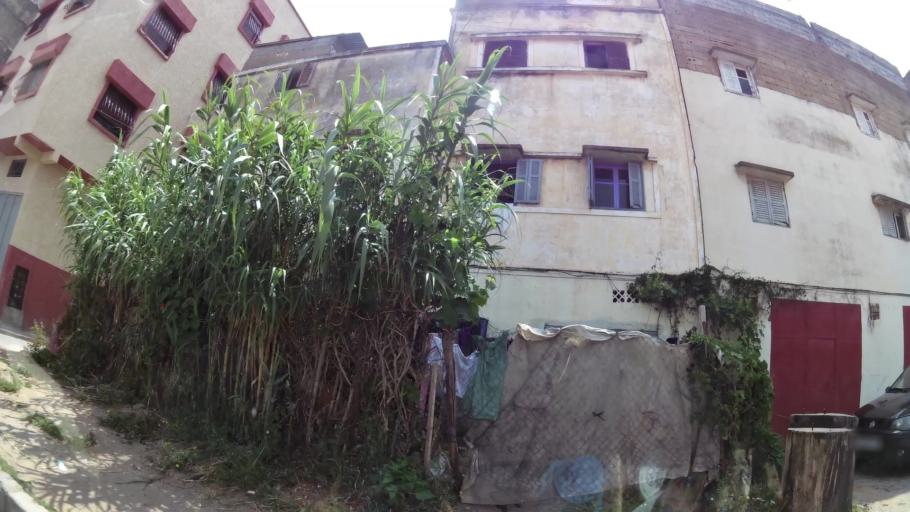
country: MA
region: Rabat-Sale-Zemmour-Zaer
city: Sale
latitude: 34.0533
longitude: -6.7823
